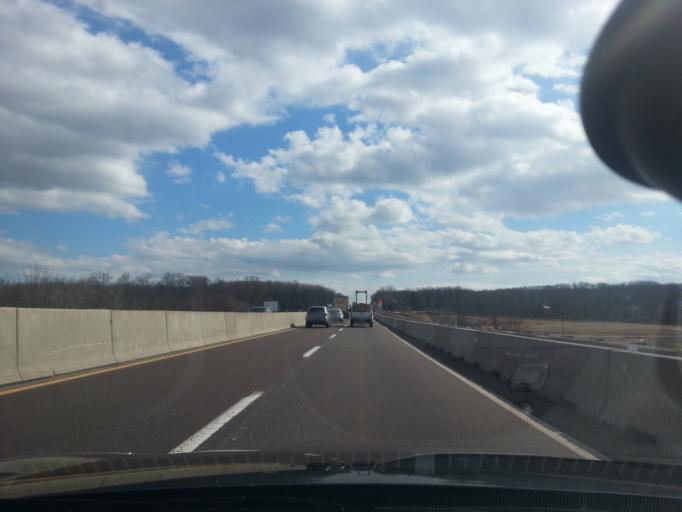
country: US
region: Pennsylvania
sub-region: Montgomery County
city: North Wales
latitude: 40.2017
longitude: -75.3192
